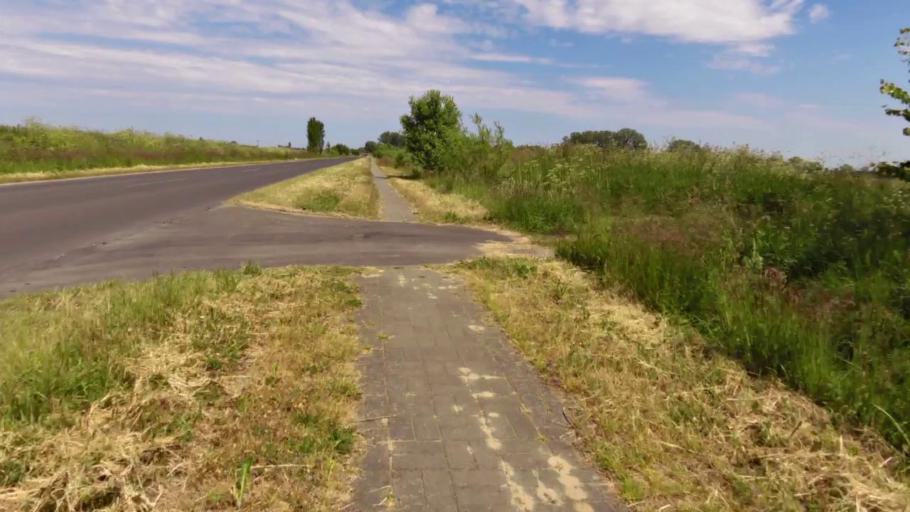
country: PL
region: West Pomeranian Voivodeship
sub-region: Powiat kamienski
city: Kamien Pomorski
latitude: 53.9531
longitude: 14.6815
